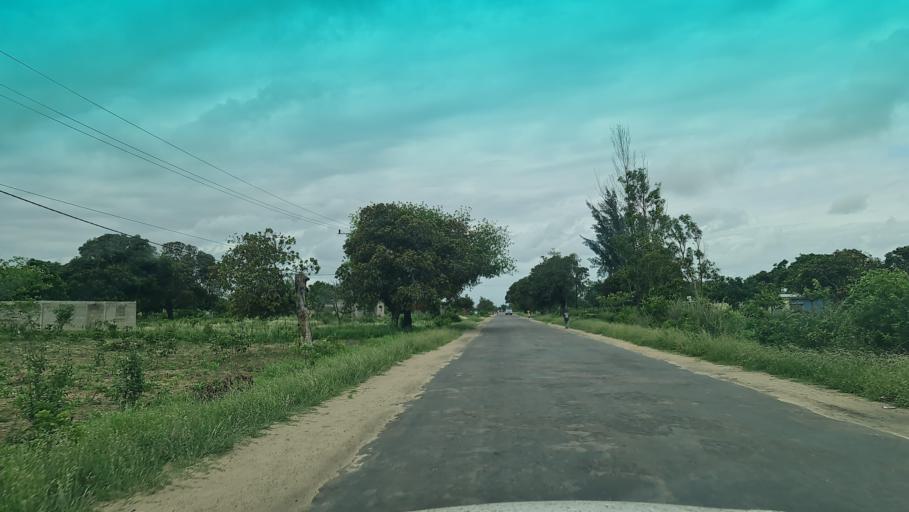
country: MZ
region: Maputo
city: Manhica
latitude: -25.4155
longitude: 32.7723
